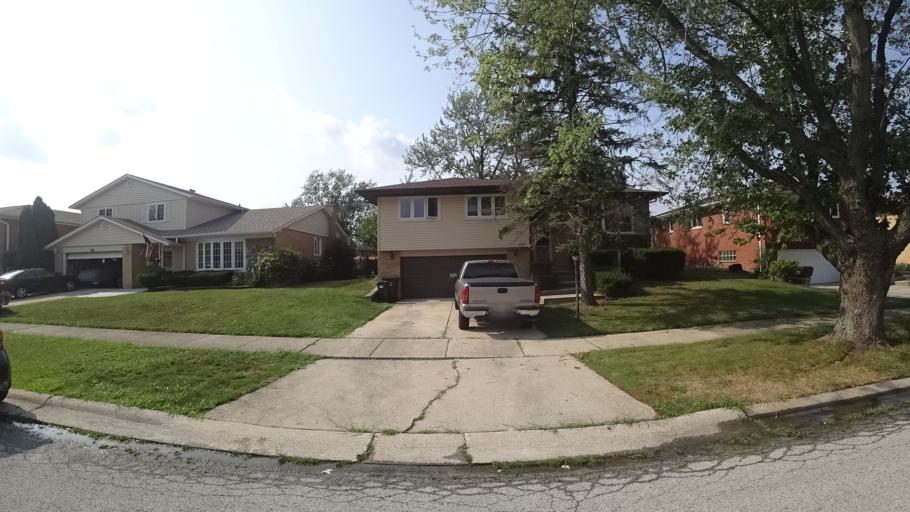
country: US
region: Illinois
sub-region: Cook County
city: Oak Forest
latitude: 41.6138
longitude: -87.7799
